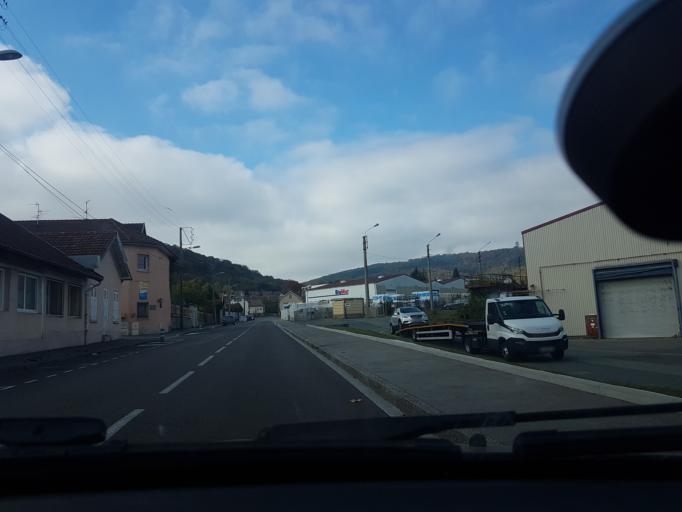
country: FR
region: Franche-Comte
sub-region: Territoire de Belfort
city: Cravanche
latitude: 47.6474
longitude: 6.8385
